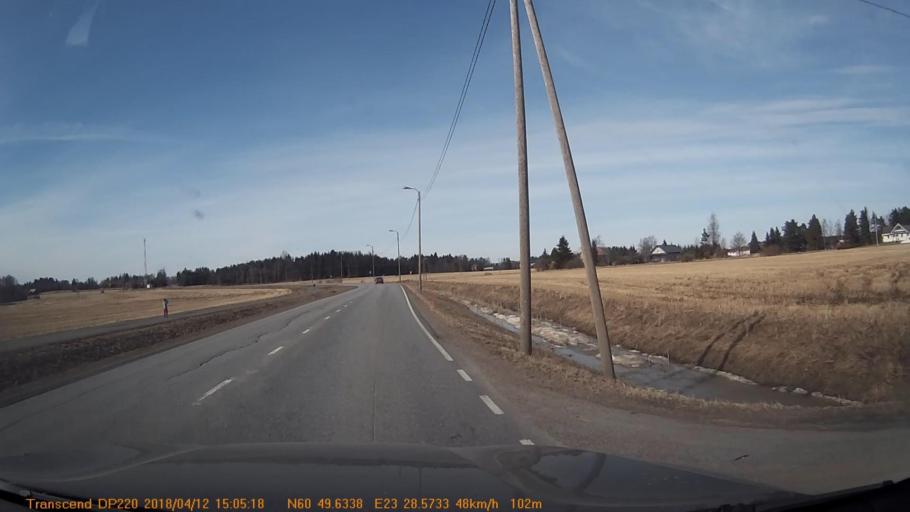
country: FI
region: Haeme
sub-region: Forssa
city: Jokioinen
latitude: 60.8274
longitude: 23.4761
